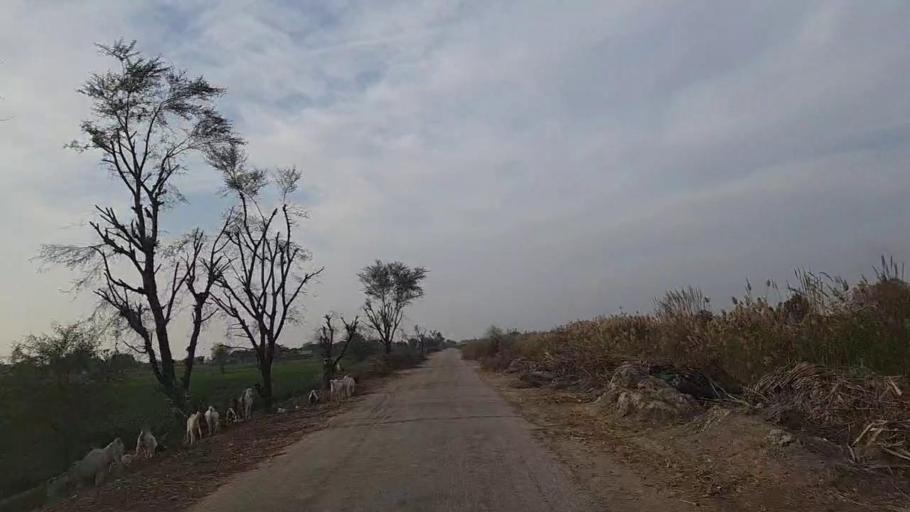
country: PK
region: Sindh
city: Daur
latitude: 26.4998
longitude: 68.4460
